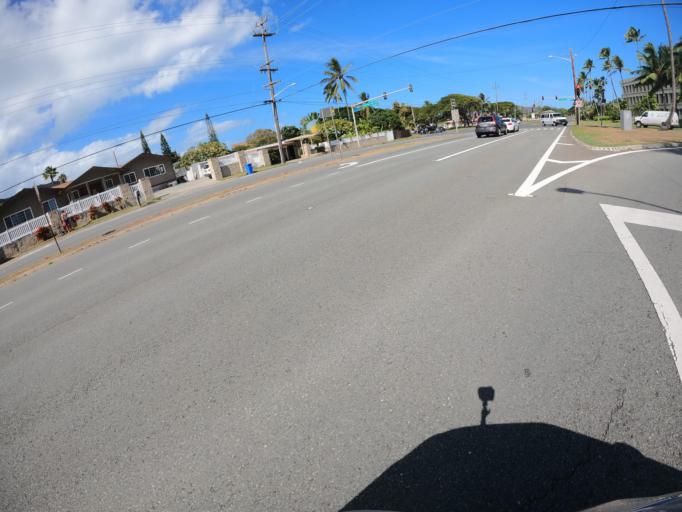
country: US
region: Hawaii
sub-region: Honolulu County
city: Kailua
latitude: 21.4207
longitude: -157.7484
